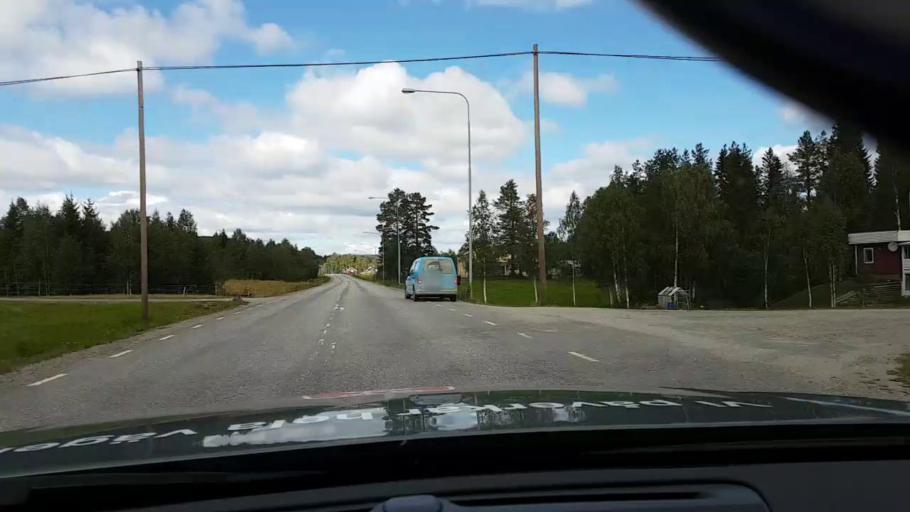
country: SE
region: Vaesternorrland
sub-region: OErnskoeldsviks Kommun
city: Bredbyn
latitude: 63.4768
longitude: 18.0945
